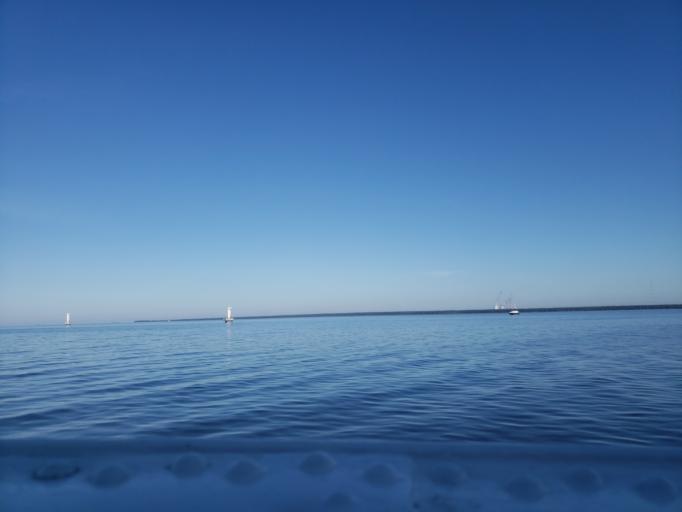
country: RU
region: St.-Petersburg
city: Lakhtinskiy
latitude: 59.9504
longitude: 30.1332
